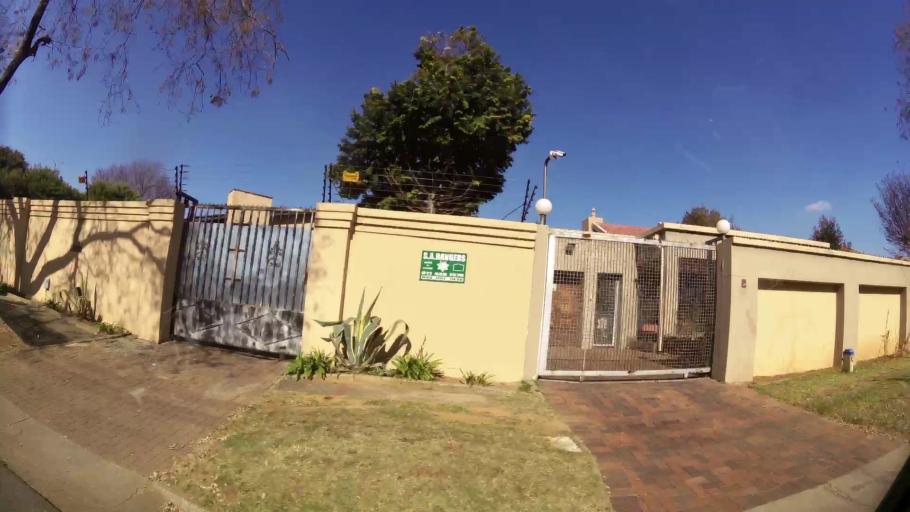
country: ZA
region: Gauteng
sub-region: City of Johannesburg Metropolitan Municipality
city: Johannesburg
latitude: -26.2538
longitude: 27.9956
